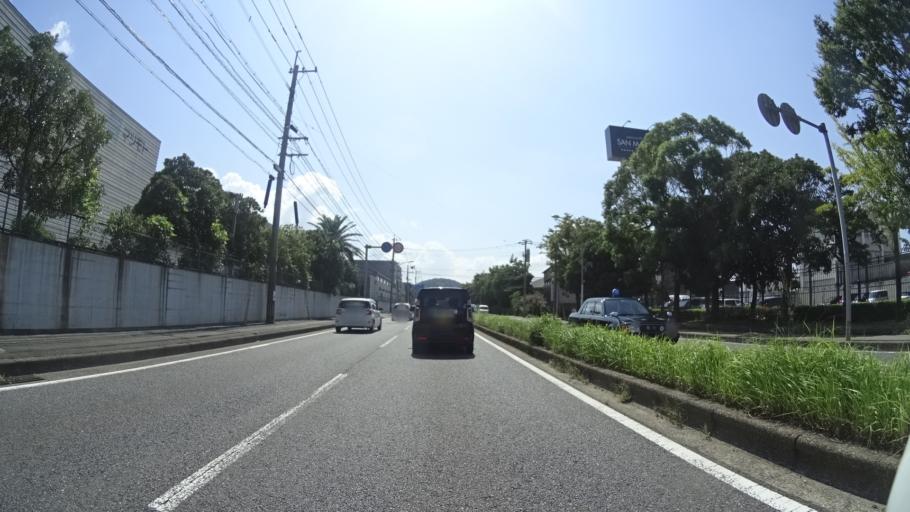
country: JP
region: Yamaguchi
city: Shimonoseki
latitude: 33.8997
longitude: 130.9237
